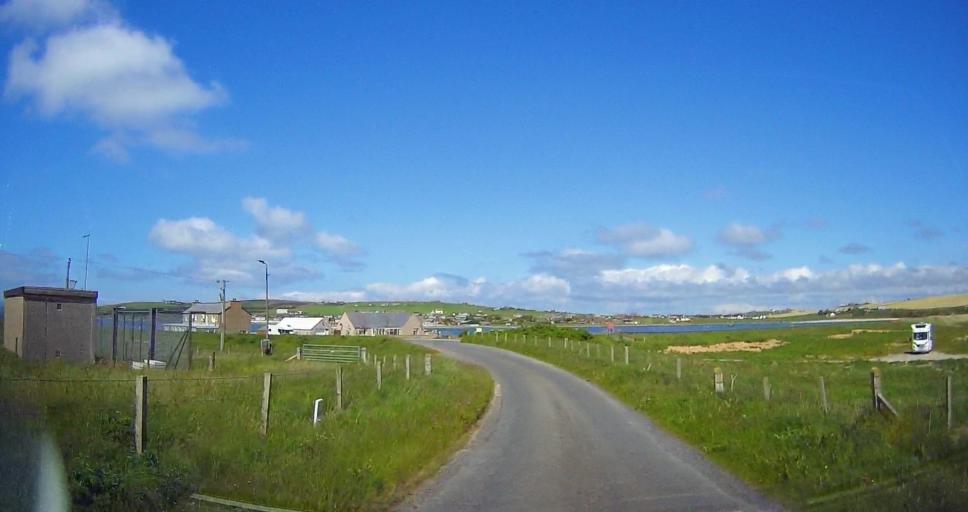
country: GB
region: Scotland
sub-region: Orkney Islands
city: Kirkwall
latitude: 58.8377
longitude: -2.9071
